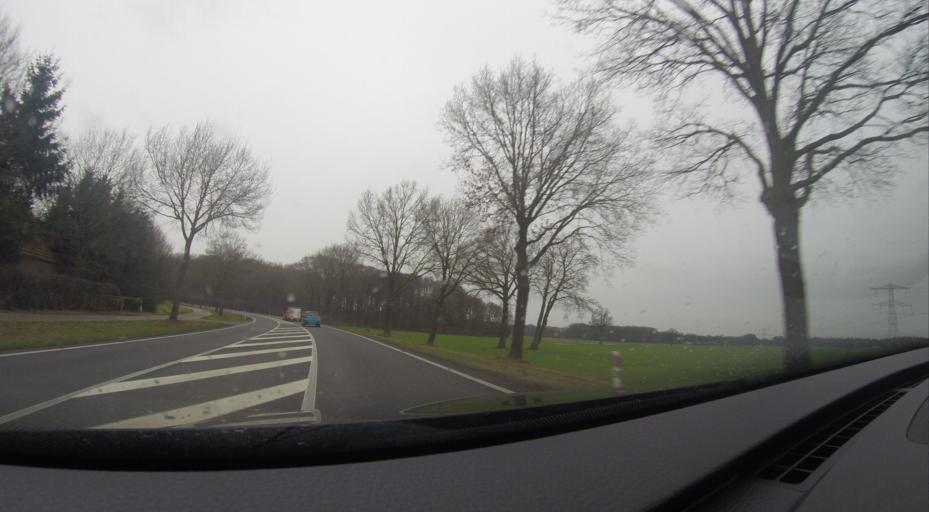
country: NL
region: Gelderland
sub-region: Gemeente Zutphen
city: Warnsveld
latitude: 52.1431
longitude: 6.2555
